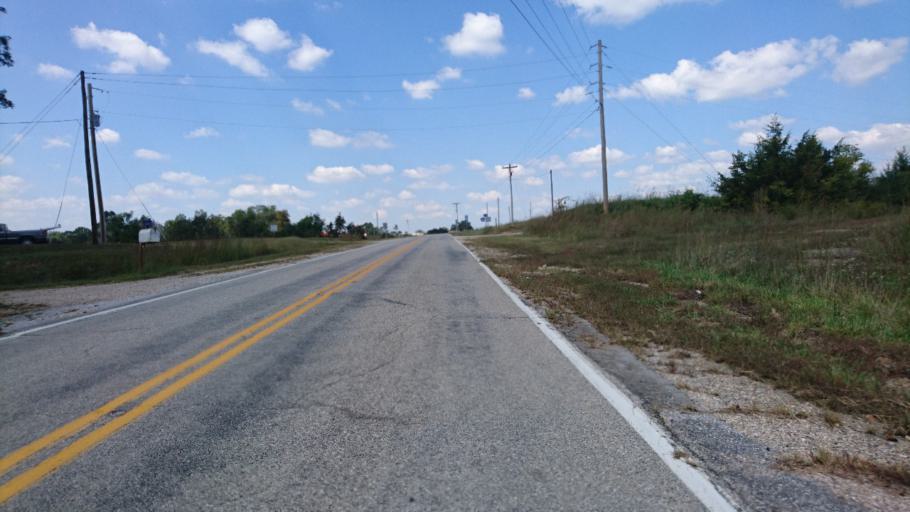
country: US
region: Missouri
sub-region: Pulaski County
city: Richland
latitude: 37.7534
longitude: -92.5044
